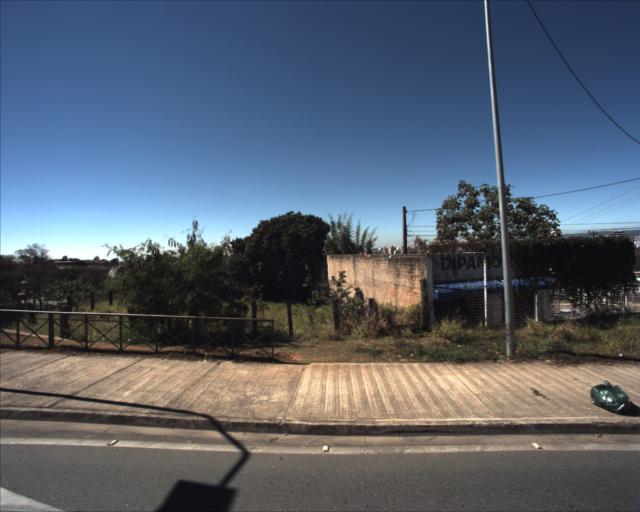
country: BR
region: Sao Paulo
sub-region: Sorocaba
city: Sorocaba
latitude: -23.5026
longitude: -47.4819
